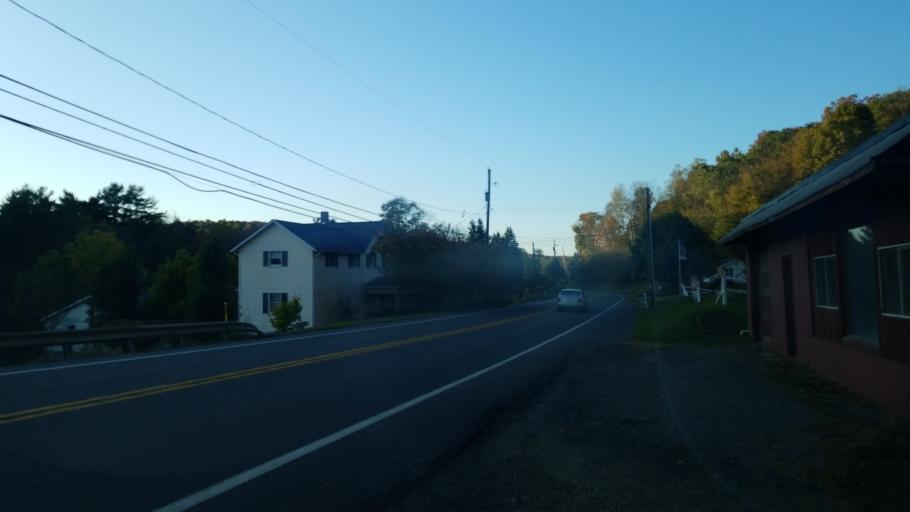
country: US
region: Pennsylvania
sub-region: Jefferson County
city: Punxsutawney
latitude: 40.9629
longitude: -78.9679
